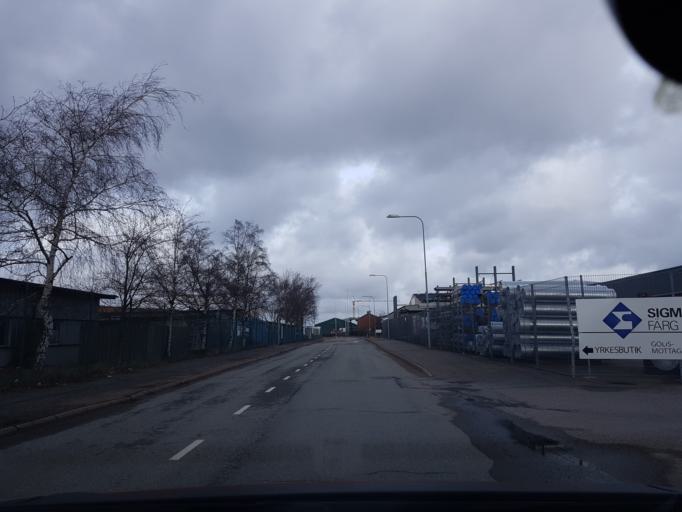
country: SE
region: Vaestra Goetaland
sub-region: Goteborg
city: Goeteborg
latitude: 57.7223
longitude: 11.9945
